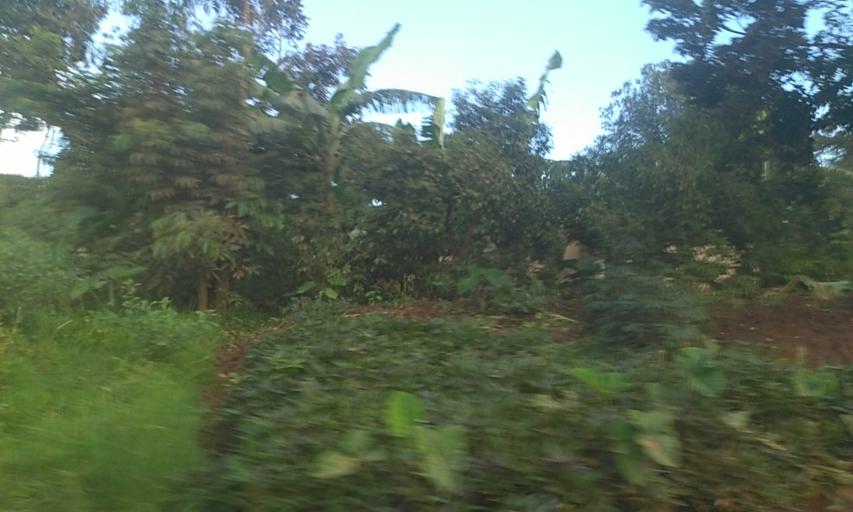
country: UG
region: Central Region
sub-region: Wakiso District
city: Kajansi
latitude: 0.2484
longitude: 32.5021
